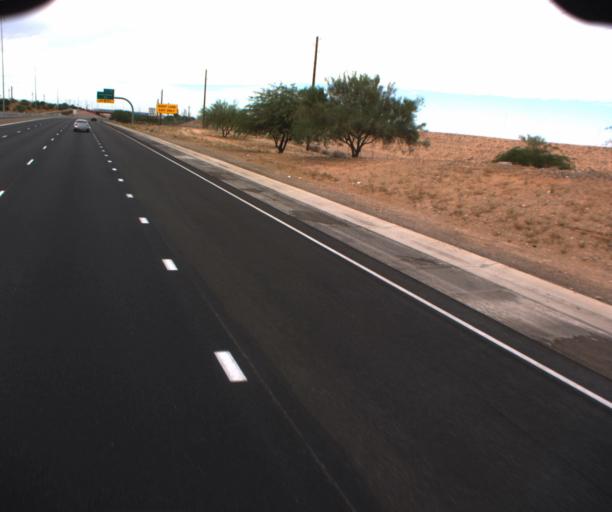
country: US
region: Arizona
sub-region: Maricopa County
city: Mesa
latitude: 33.4814
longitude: -111.7269
